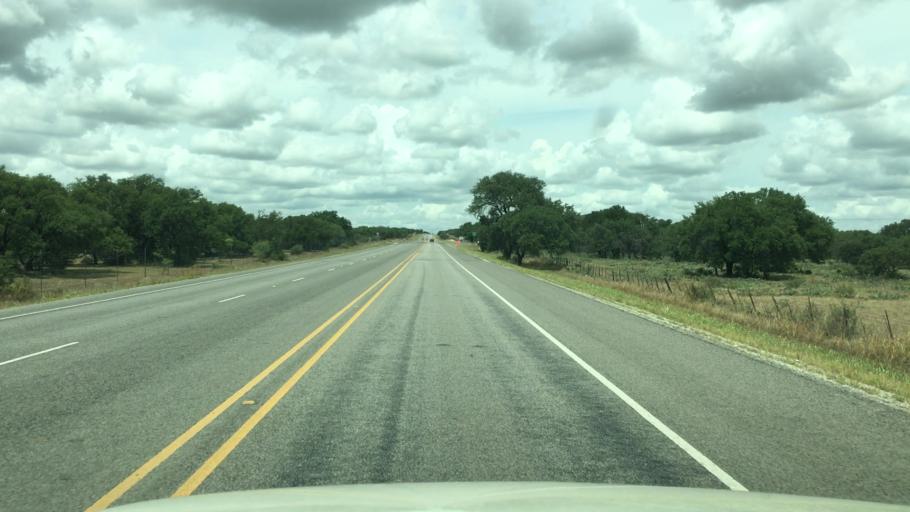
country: US
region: Texas
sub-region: McCulloch County
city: Brady
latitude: 31.0259
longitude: -99.2227
